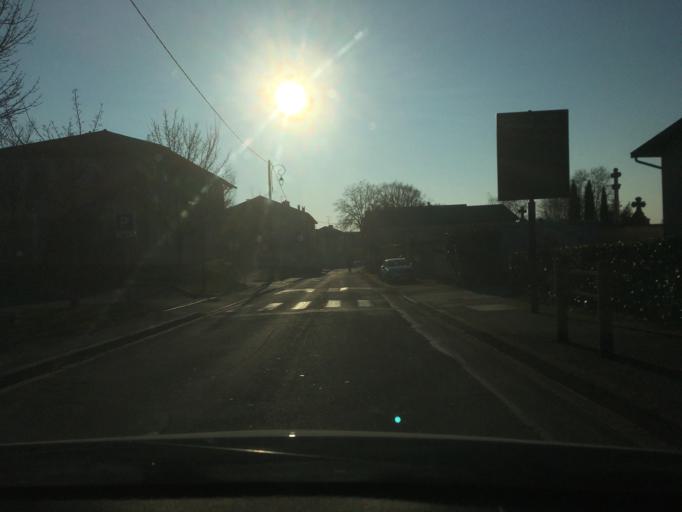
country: FR
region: Rhone-Alpes
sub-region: Departement de l'Ain
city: Ars-sur-Formans
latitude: 45.9944
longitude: 4.8193
